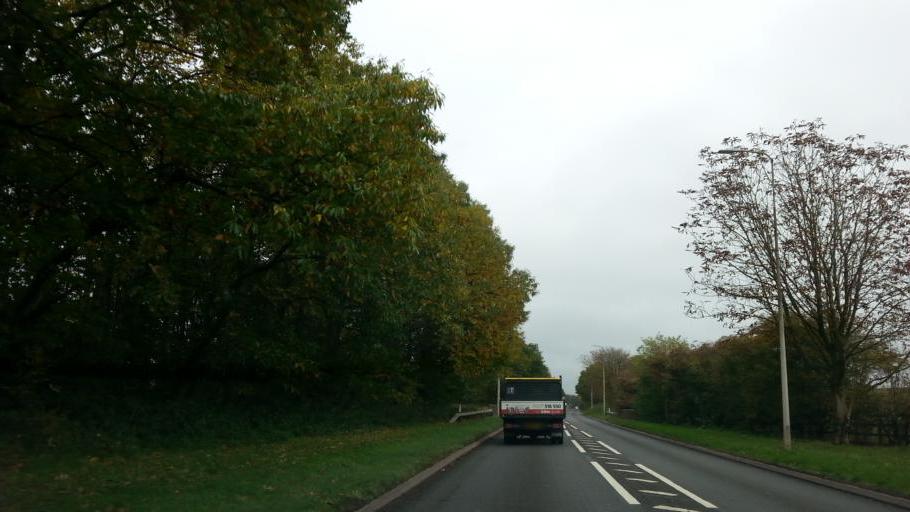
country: GB
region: England
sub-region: Worcestershire
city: Bromsgrove
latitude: 52.3435
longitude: -2.0485
